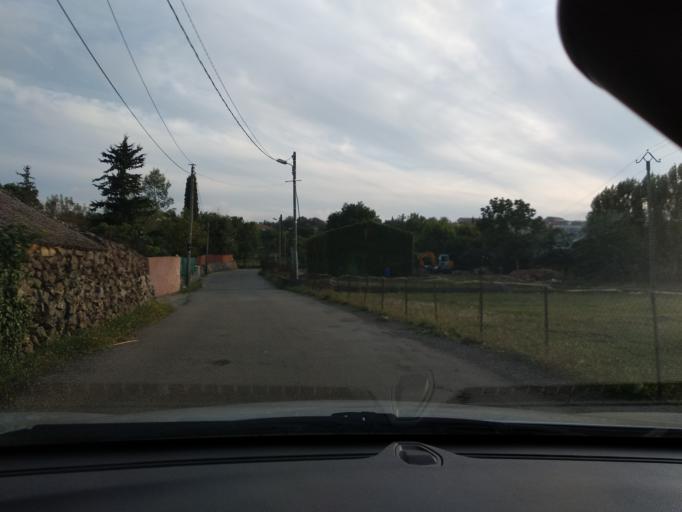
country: FR
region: Provence-Alpes-Cote d'Azur
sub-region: Departement des Alpes-Maritimes
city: Saint-Cezaire-sur-Siagne
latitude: 43.6525
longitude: 6.7994
